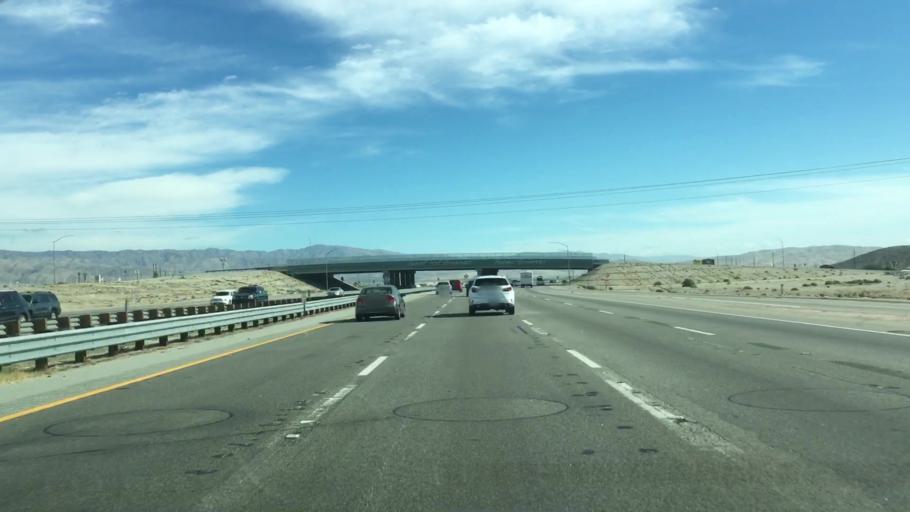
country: US
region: California
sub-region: Riverside County
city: Garnet
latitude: 33.9047
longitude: -116.5484
